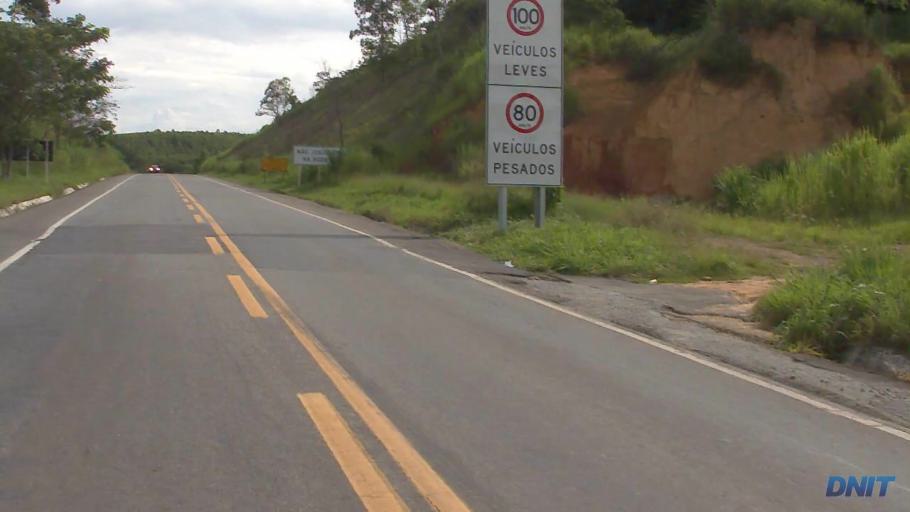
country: BR
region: Minas Gerais
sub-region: Belo Oriente
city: Belo Oriente
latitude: -19.2458
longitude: -42.3375
